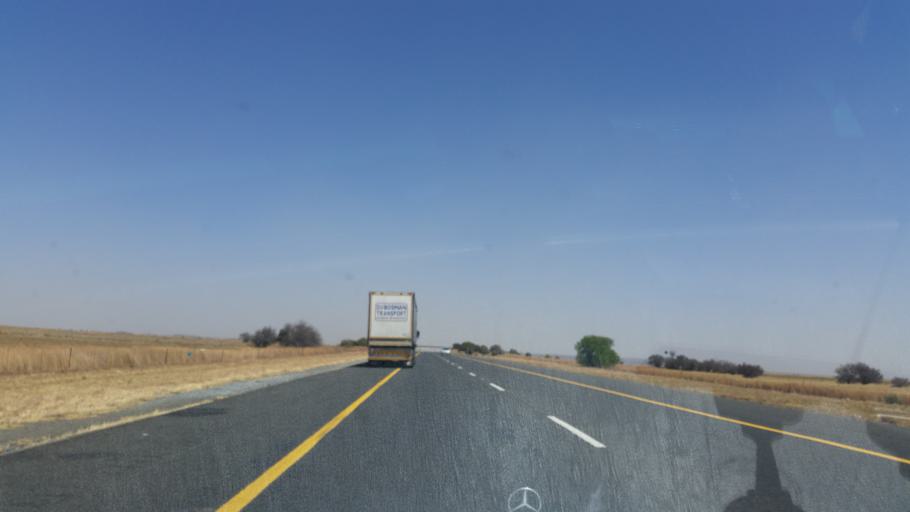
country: ZA
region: Orange Free State
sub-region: Lejweleputswa District Municipality
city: Winburg
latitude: -28.6492
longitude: 26.8776
